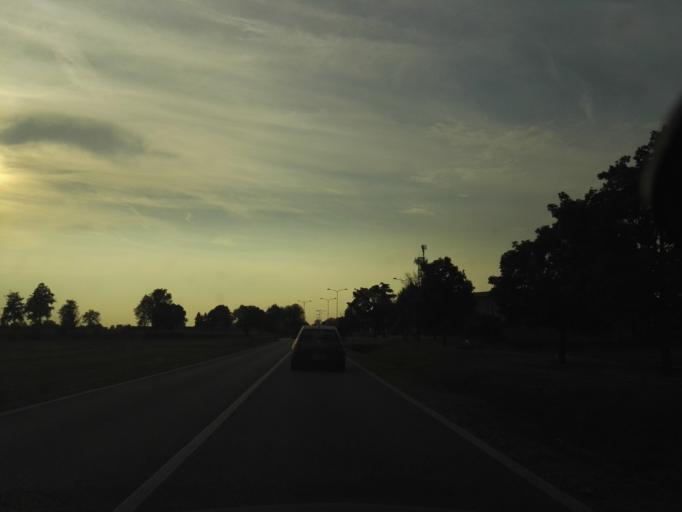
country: IT
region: Lombardy
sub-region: Citta metropolitana di Milano
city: Bettola-Zeloforomagno
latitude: 45.4345
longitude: 9.3023
